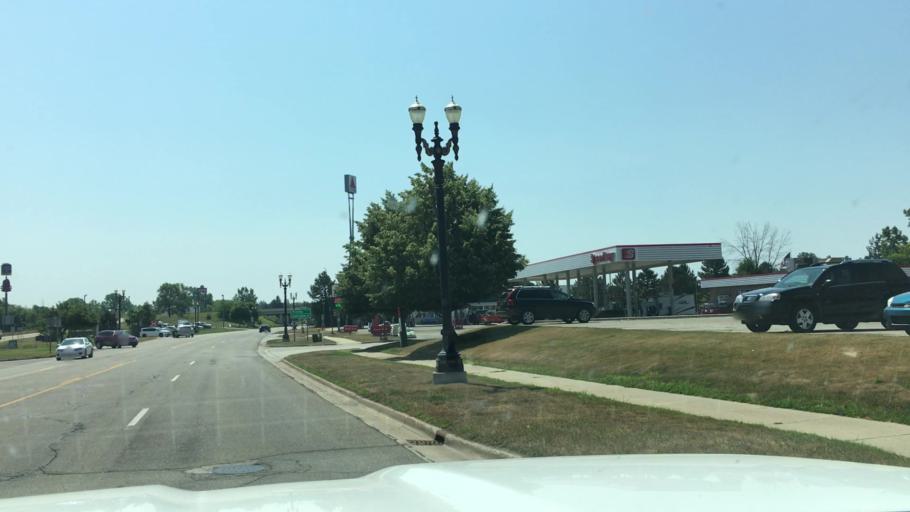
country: US
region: Michigan
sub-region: Ionia County
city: Portland
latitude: 42.8624
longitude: -84.8871
